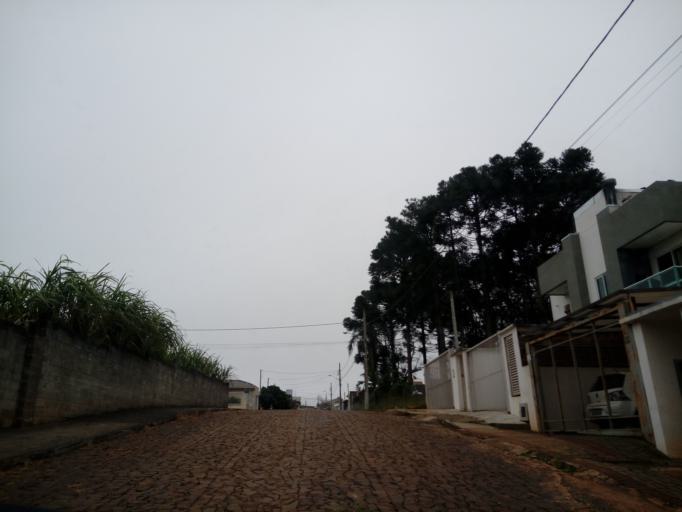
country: BR
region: Santa Catarina
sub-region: Chapeco
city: Chapeco
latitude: -27.1074
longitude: -52.6687
